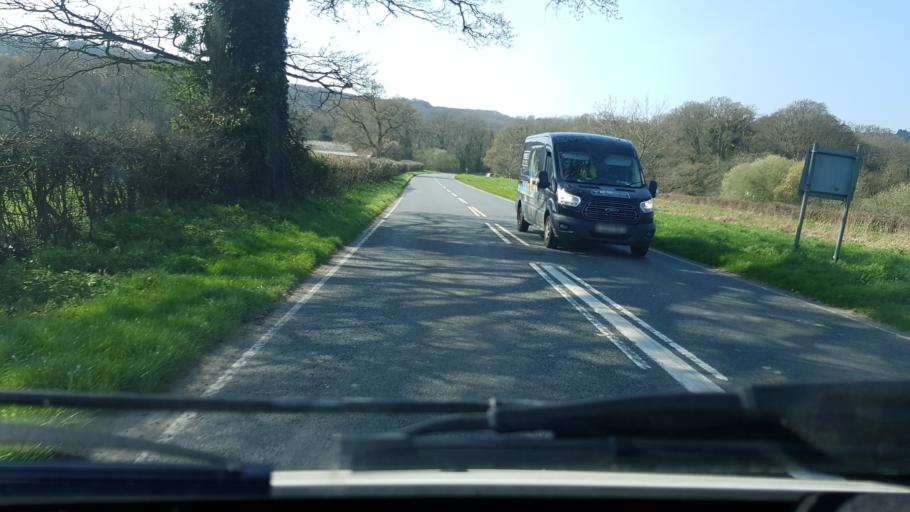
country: GB
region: England
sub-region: West Sussex
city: Fernhurst
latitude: 51.0331
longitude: -0.7277
